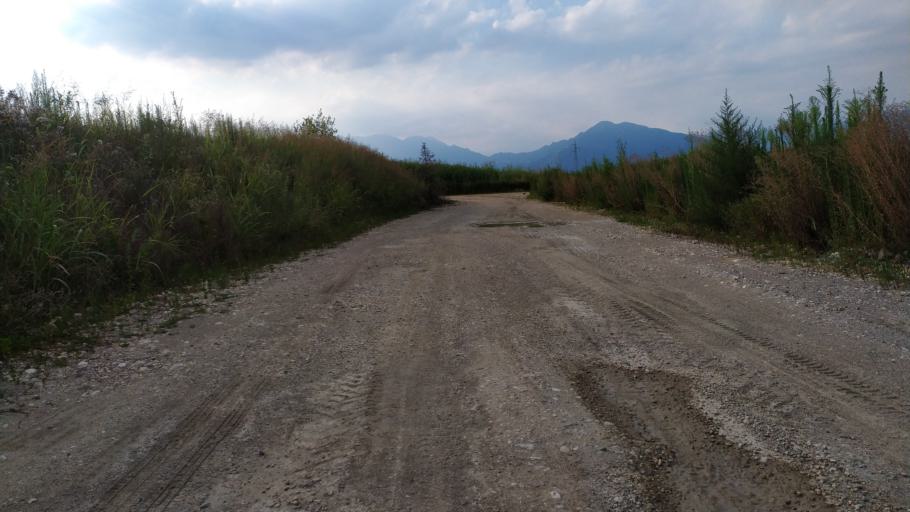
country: IT
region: Veneto
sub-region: Provincia di Vicenza
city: Isola Vicentina
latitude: 45.6505
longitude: 11.4384
